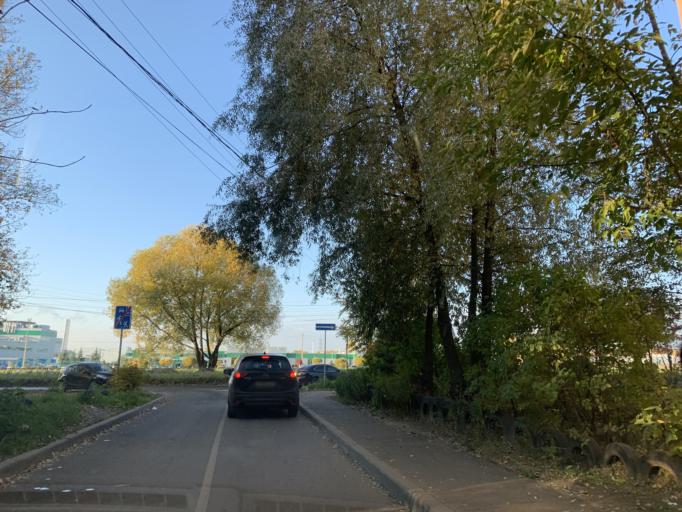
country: RU
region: Jaroslavl
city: Yaroslavl
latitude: 57.6810
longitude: 39.7639
